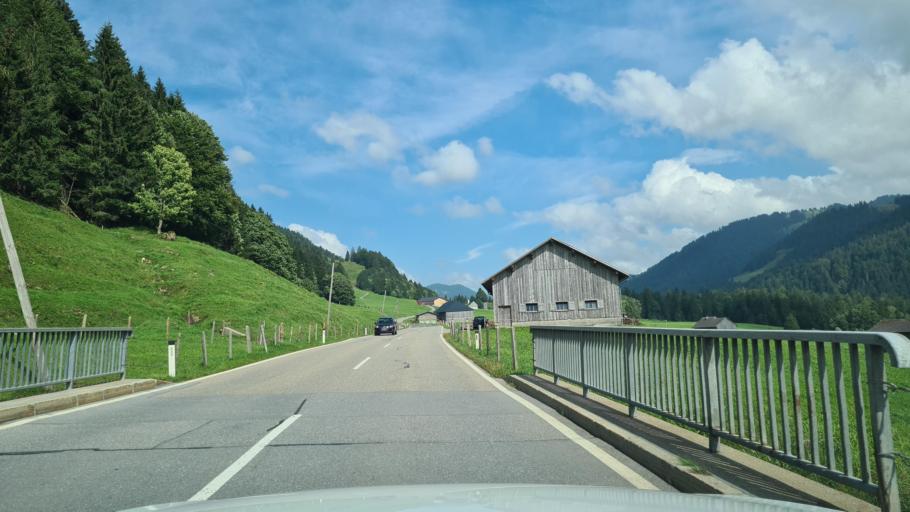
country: AT
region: Vorarlberg
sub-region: Politischer Bezirk Bregenz
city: Sibratsgfall
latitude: 47.4498
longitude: 10.0266
